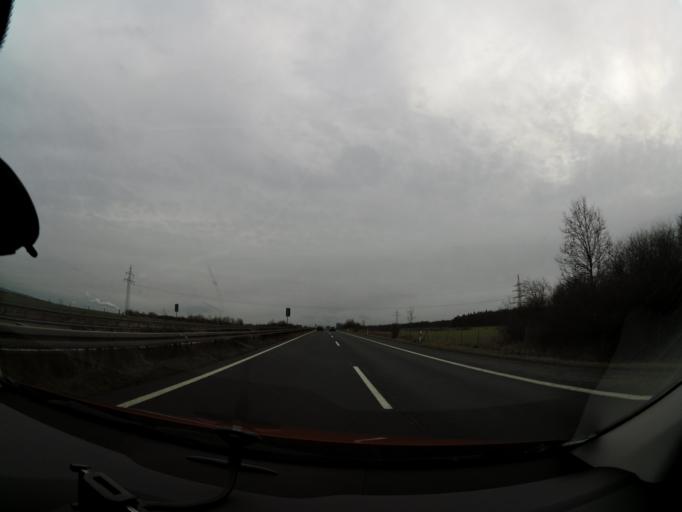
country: DE
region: Lower Saxony
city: Gielde
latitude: 52.0361
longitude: 10.5154
